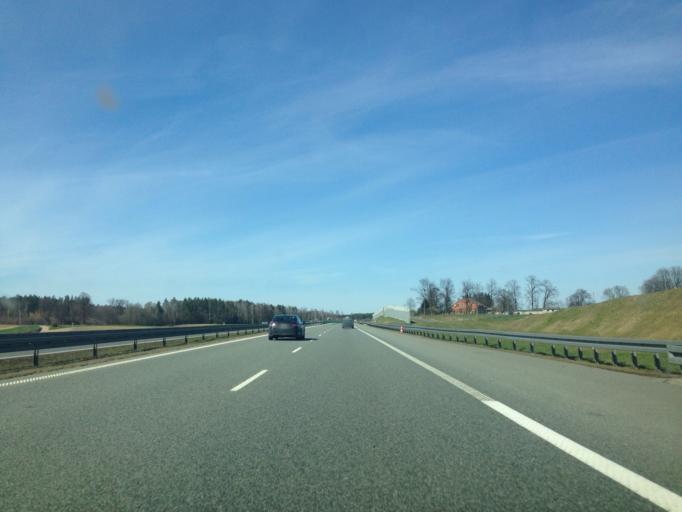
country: PL
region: Pomeranian Voivodeship
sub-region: Powiat starogardzki
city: Bobowo
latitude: 53.8706
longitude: 18.6288
